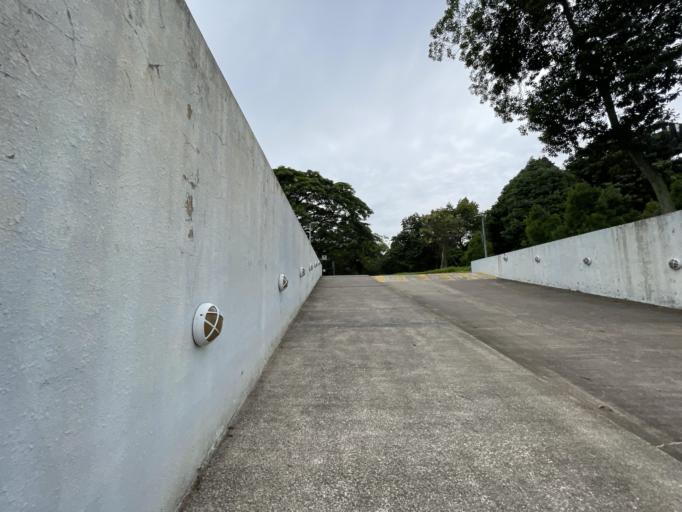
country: SG
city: Singapore
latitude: 1.2910
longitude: 103.7673
